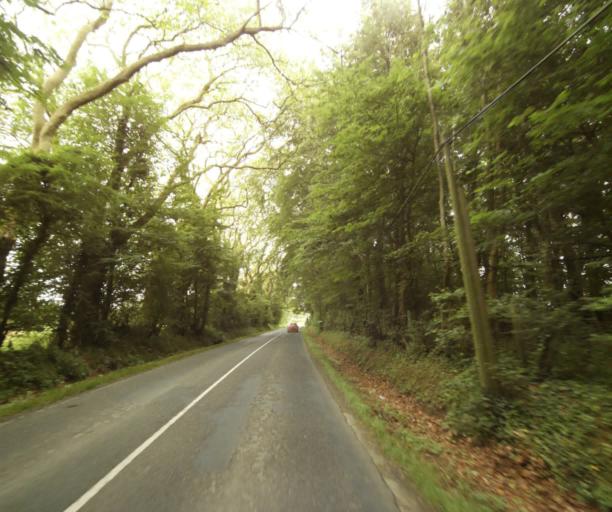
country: FR
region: Lower Normandy
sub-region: Departement du Calvados
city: Houlgate
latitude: 49.2794
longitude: -0.0743
